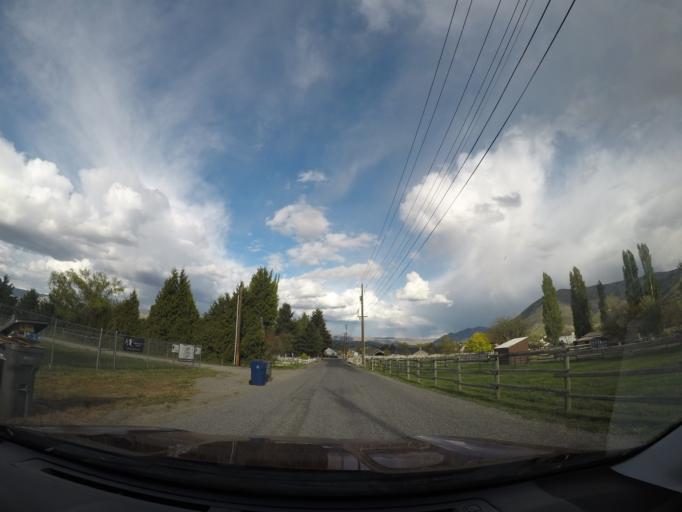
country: US
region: Washington
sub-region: Chelan County
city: South Wenatchee
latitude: 47.3969
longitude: -120.3157
